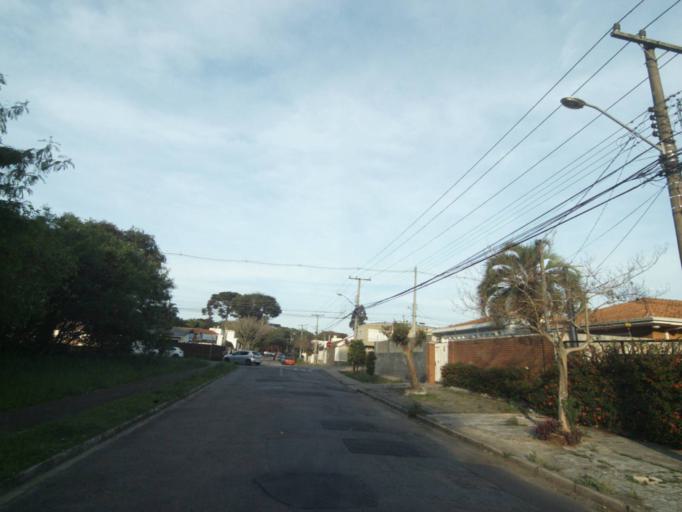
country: BR
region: Parana
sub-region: Curitiba
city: Curitiba
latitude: -25.4546
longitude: -49.3060
